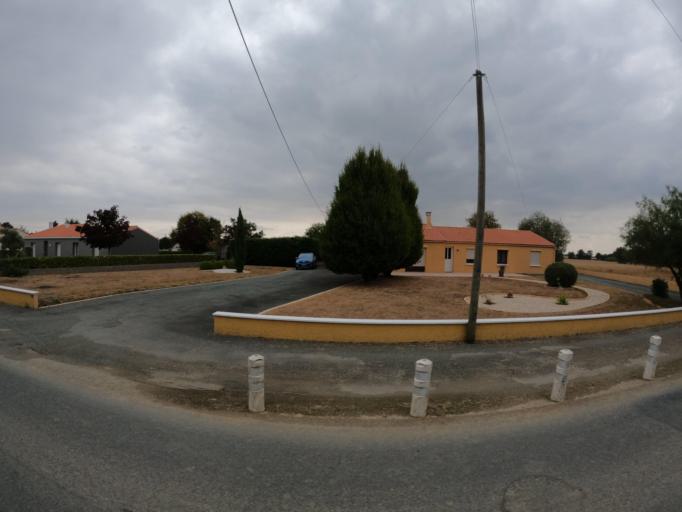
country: FR
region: Pays de la Loire
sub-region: Departement de la Vendee
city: La Guyonniere
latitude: 46.9755
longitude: -1.2419
